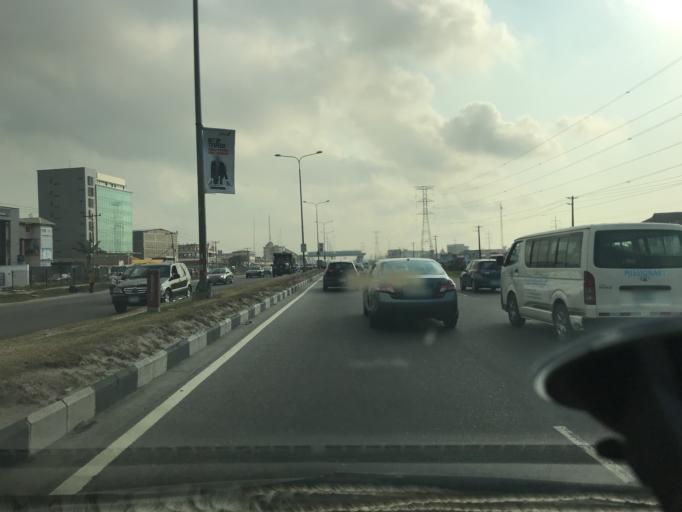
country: NG
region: Lagos
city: Ikoyi
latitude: 6.4372
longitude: 3.5122
